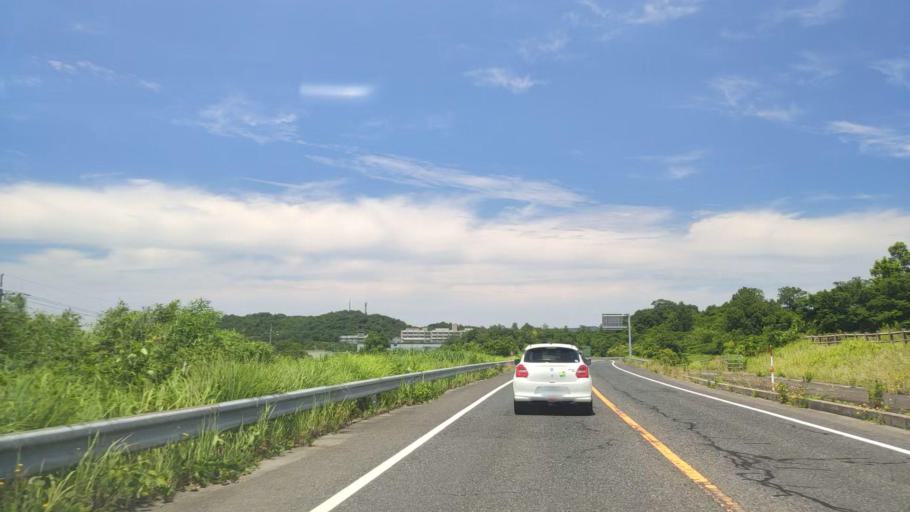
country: JP
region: Tottori
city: Tottori
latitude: 35.4437
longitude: 134.2558
